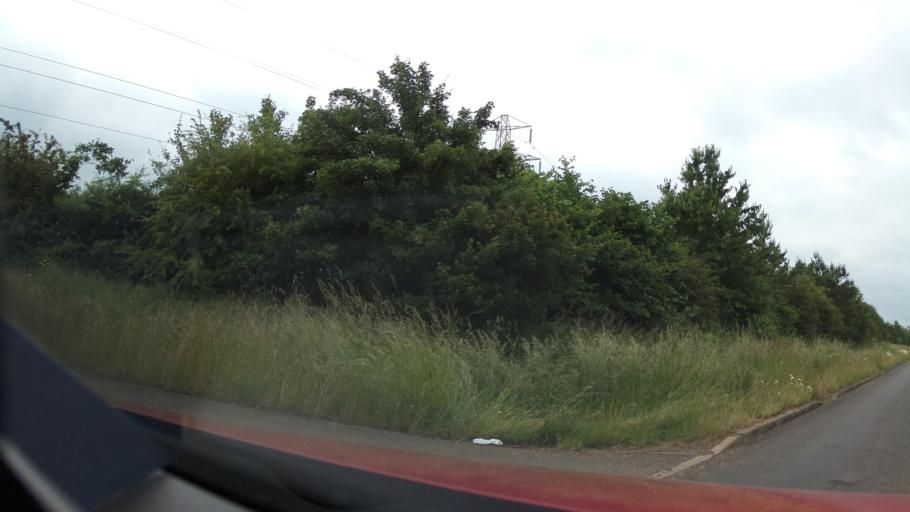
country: GB
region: England
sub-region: District of Rutland
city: Oakham
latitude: 52.6639
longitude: -0.7146
